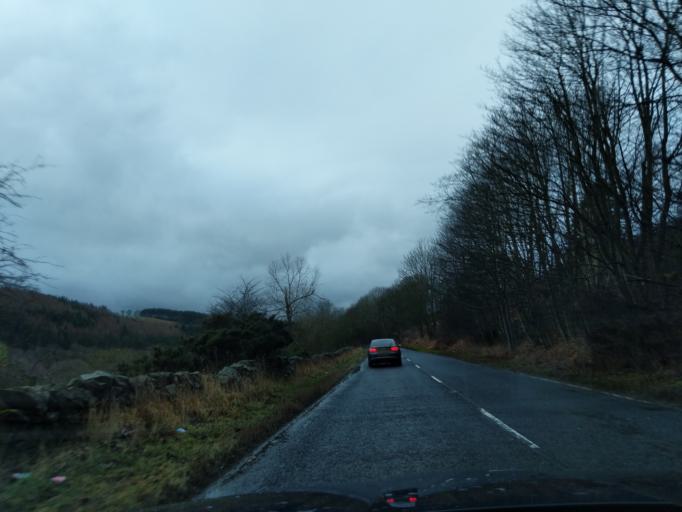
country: GB
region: Scotland
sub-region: The Scottish Borders
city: Galashiels
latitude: 55.6415
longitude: -2.8383
